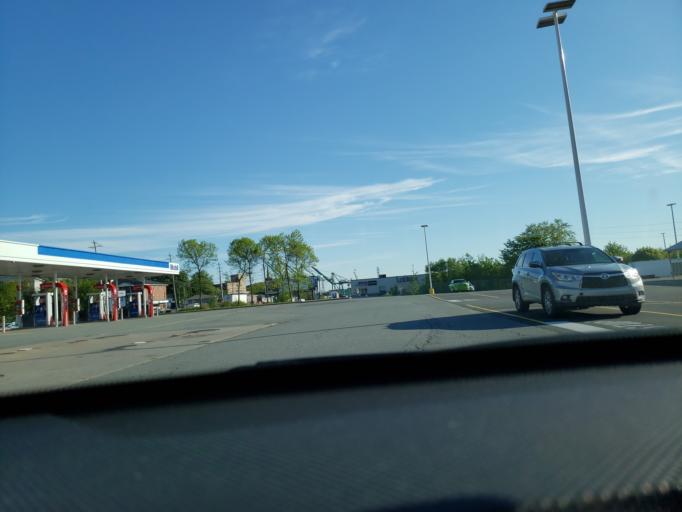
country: CA
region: Nova Scotia
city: Dartmouth
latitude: 44.6581
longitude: -63.6285
